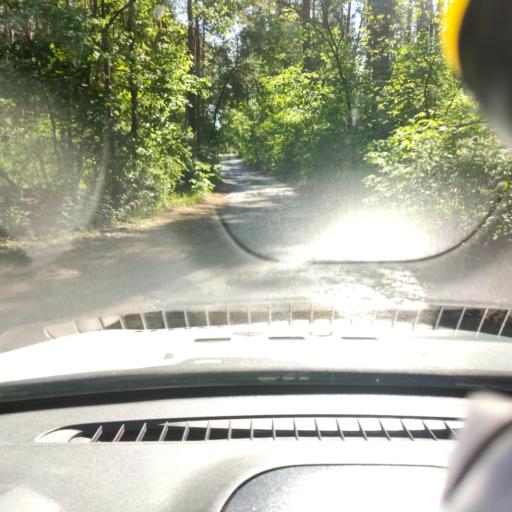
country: RU
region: Samara
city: Tol'yatti
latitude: 53.4686
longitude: 49.3877
